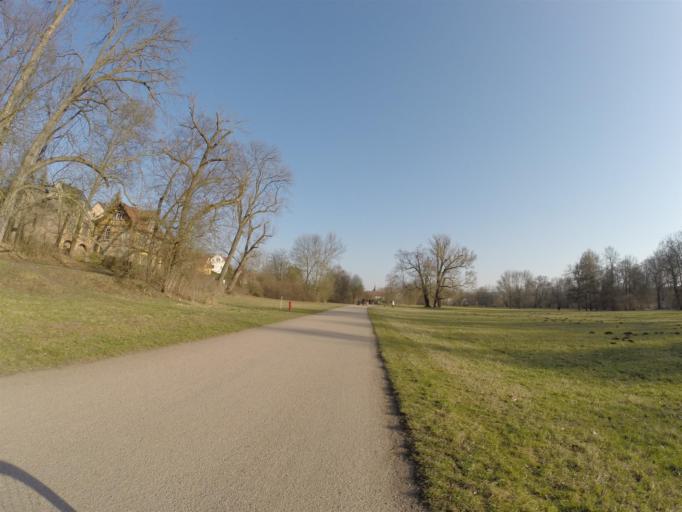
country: DE
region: Thuringia
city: Weimar
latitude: 50.9686
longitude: 11.3405
